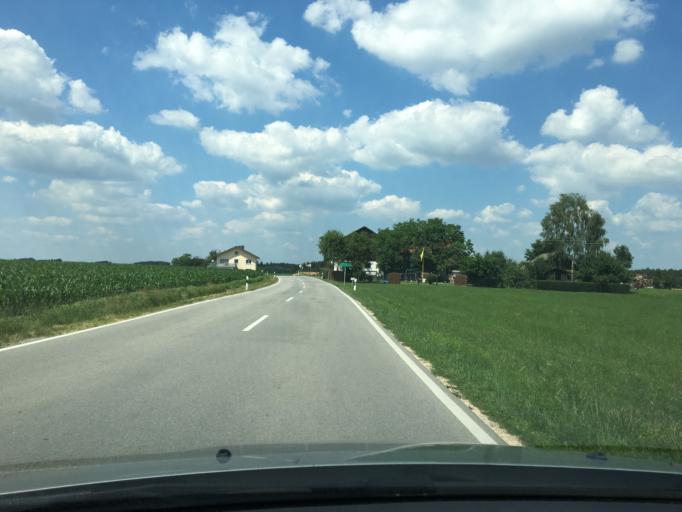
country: DE
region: Bavaria
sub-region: Upper Bavaria
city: Neumarkt-Sankt Veit
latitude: 48.3760
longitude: 12.5066
